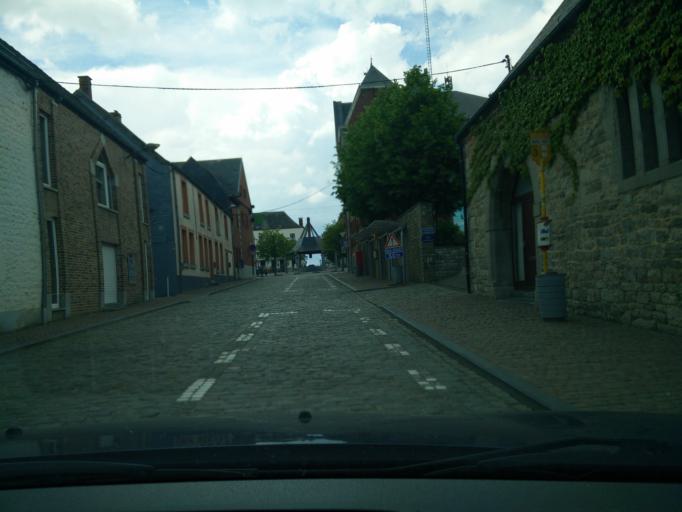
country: BE
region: Wallonia
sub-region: Province de Namur
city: Philippeville
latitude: 50.1955
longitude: 4.5441
